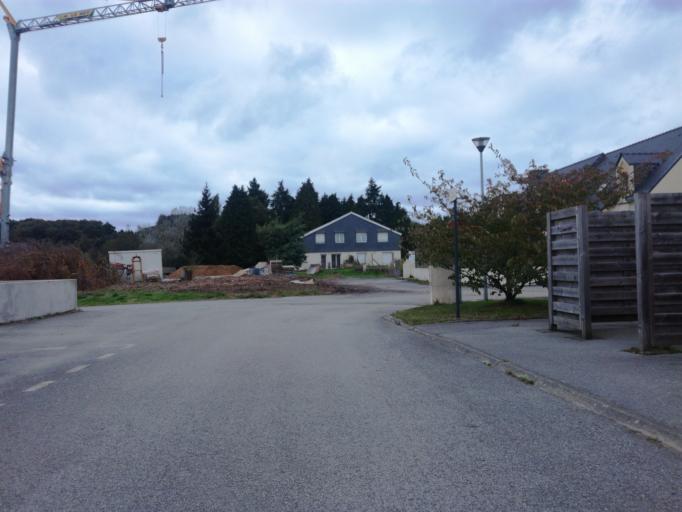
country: FR
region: Brittany
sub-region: Departement du Morbihan
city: Le Sourn
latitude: 48.0402
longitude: -2.9875
